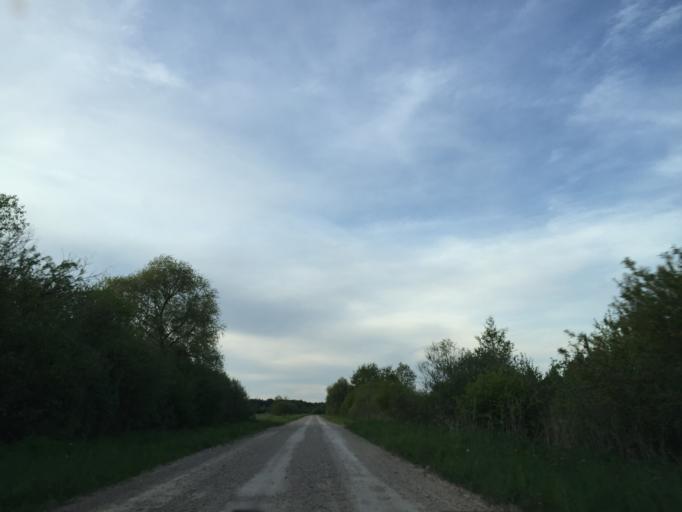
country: LV
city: Tireli
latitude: 56.7695
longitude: 23.5427
